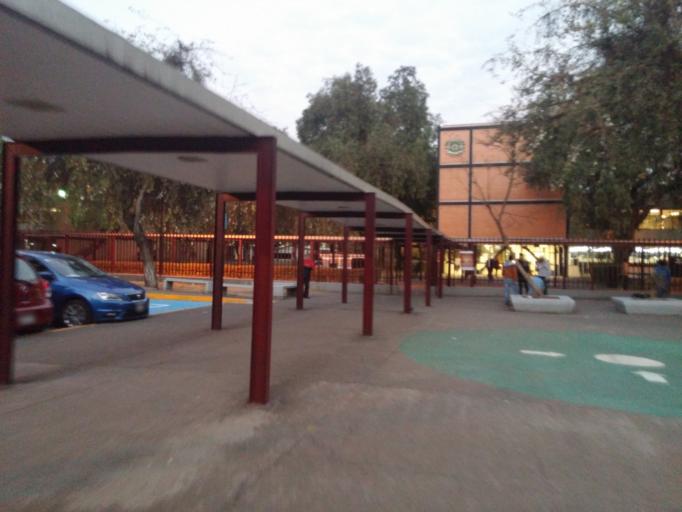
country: MX
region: Mexico
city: Colonia Lindavista
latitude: 19.4997
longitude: -99.1358
